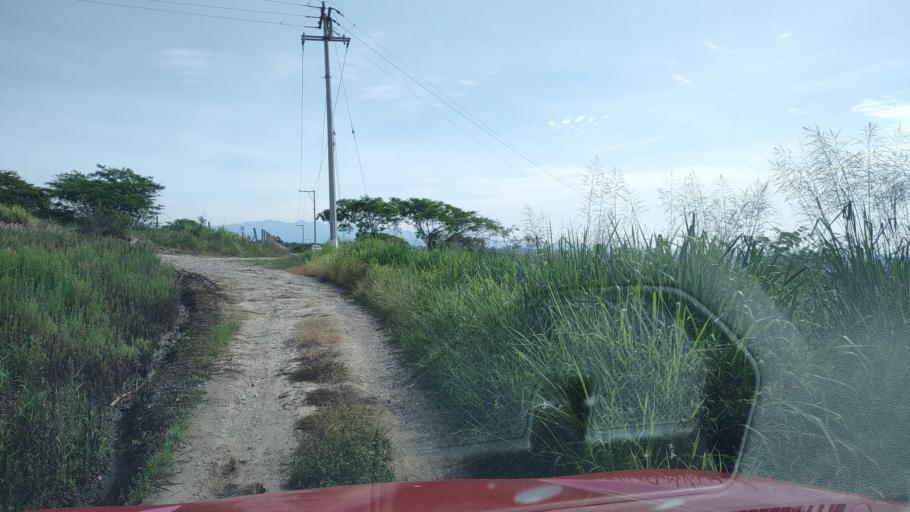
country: MX
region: Veracruz
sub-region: Emiliano Zapata
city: Dos Rios
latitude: 19.4717
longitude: -96.8229
